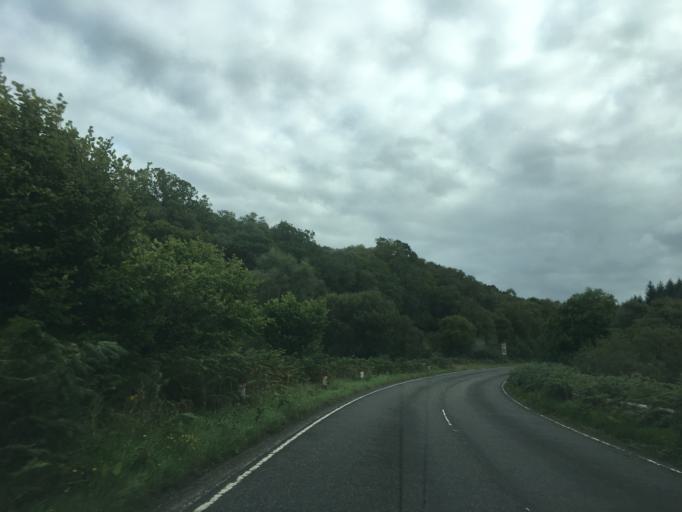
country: GB
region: Scotland
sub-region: Argyll and Bute
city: Oban
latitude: 56.3365
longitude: -5.5126
